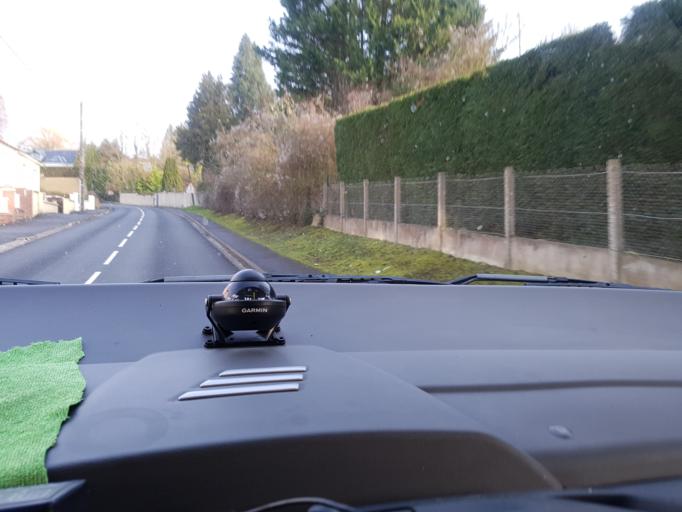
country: FR
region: Champagne-Ardenne
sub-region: Departement des Ardennes
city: Warcq
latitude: 49.7777
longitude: 4.6931
